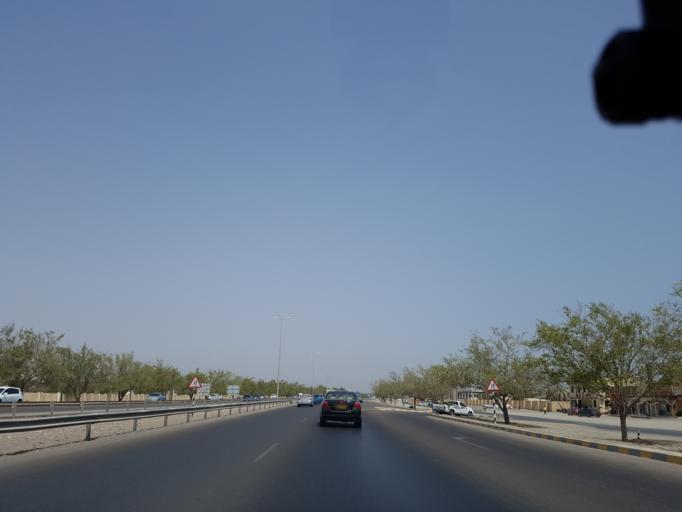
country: OM
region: Al Batinah
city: Saham
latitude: 24.1461
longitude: 56.8726
